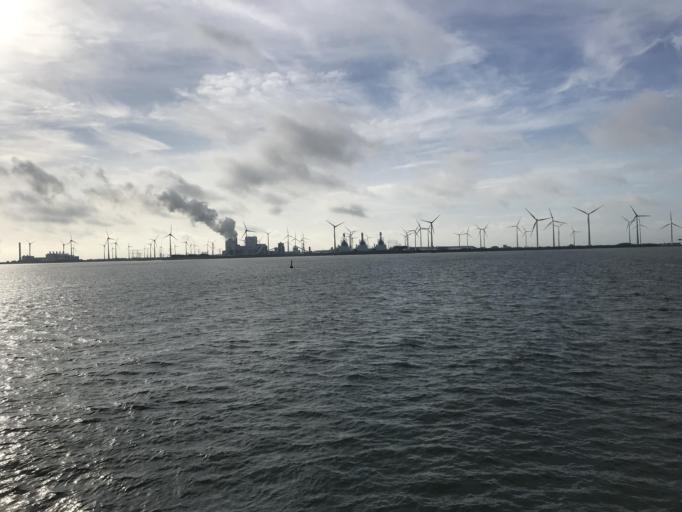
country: NL
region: Groningen
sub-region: Gemeente Appingedam
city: Appingedam
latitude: 53.4695
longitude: 6.8625
